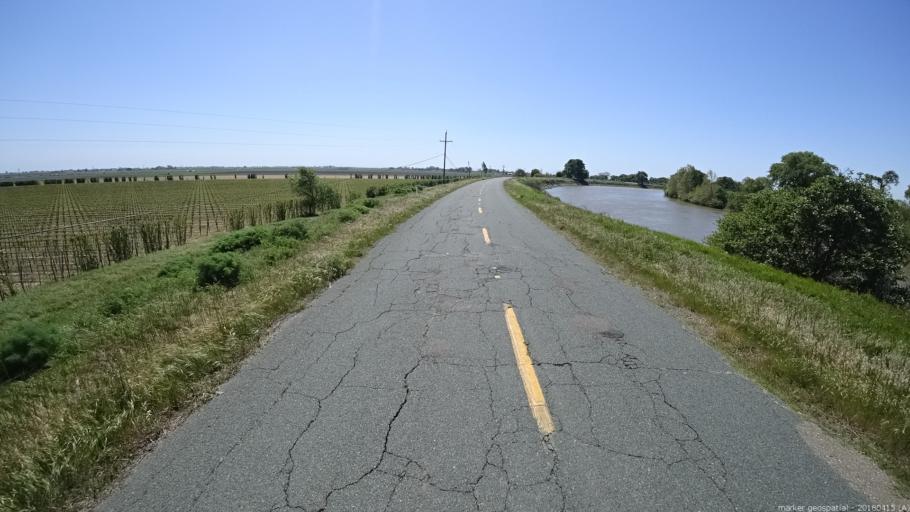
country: US
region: California
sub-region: Sacramento County
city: Walnut Grove
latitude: 38.2573
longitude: -121.5940
